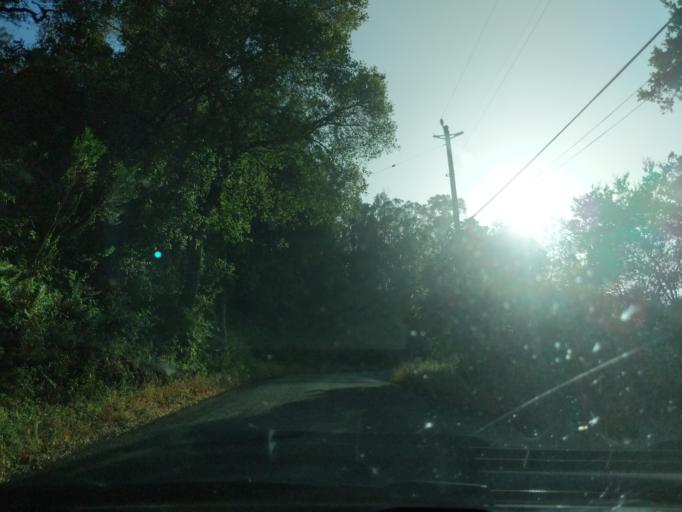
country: US
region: California
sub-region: Monterey County
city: Las Lomas
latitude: 36.8933
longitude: -121.6973
